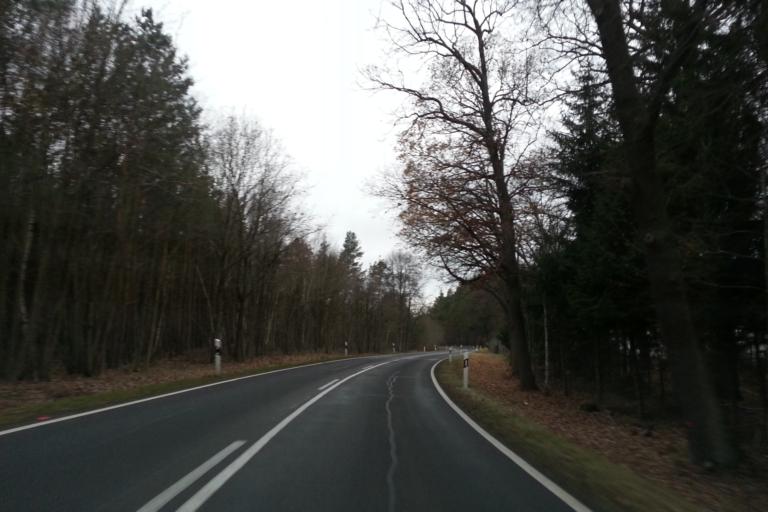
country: DE
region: Mecklenburg-Vorpommern
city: Jatznick
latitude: 53.6034
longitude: 13.9298
